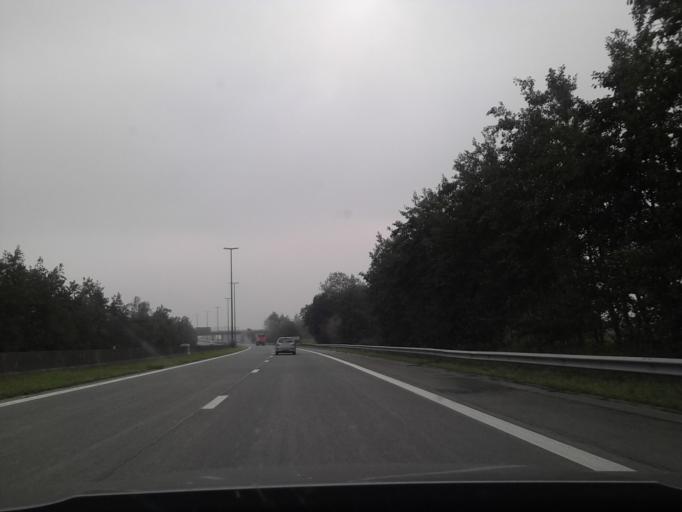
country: BE
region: Wallonia
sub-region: Province du Hainaut
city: Lessines
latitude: 50.6709
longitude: 3.8528
